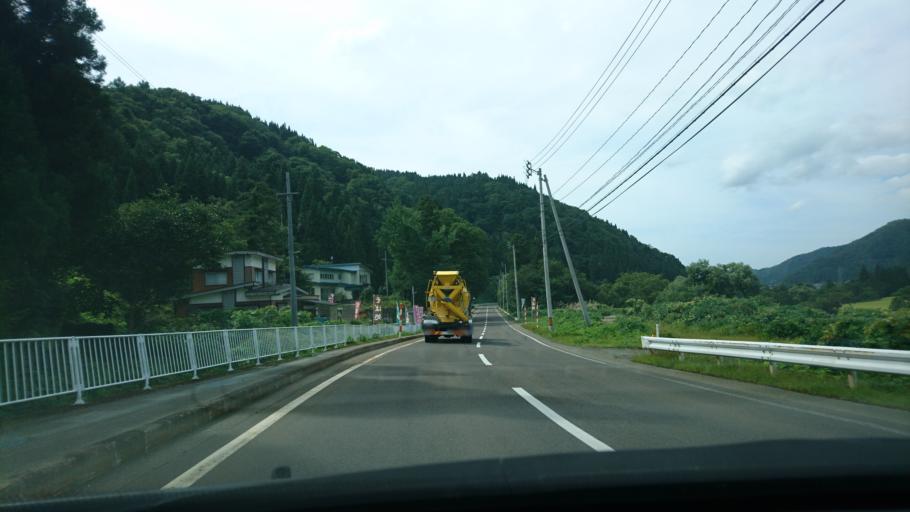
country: JP
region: Akita
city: Yuzawa
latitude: 39.1729
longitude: 140.6730
